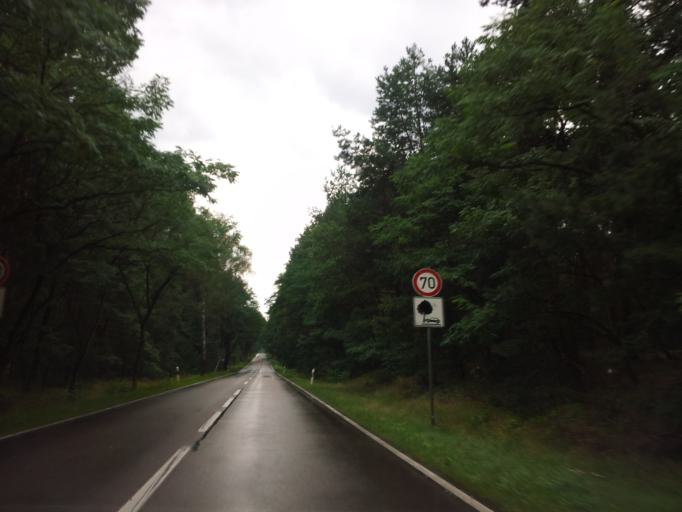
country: DE
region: Brandenburg
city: Graben
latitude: 52.2567
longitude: 12.4426
